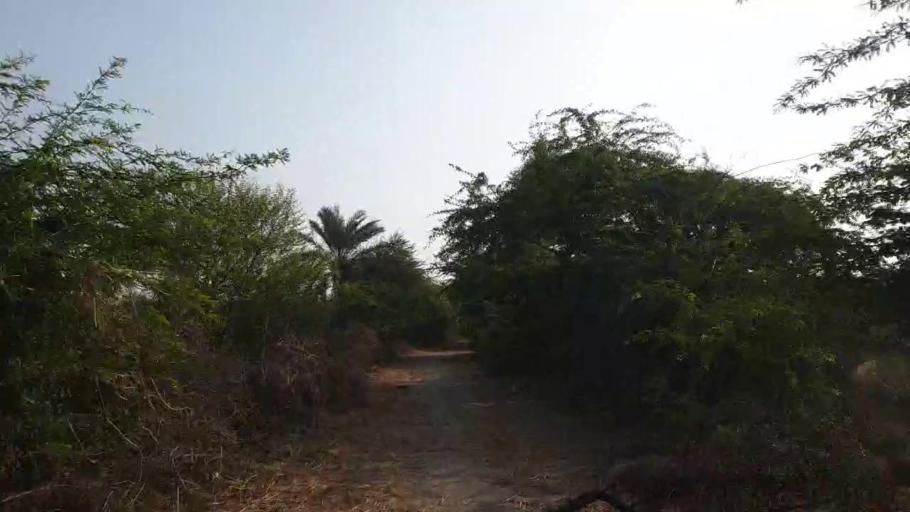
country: PK
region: Sindh
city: Kario
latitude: 24.8979
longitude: 68.5673
